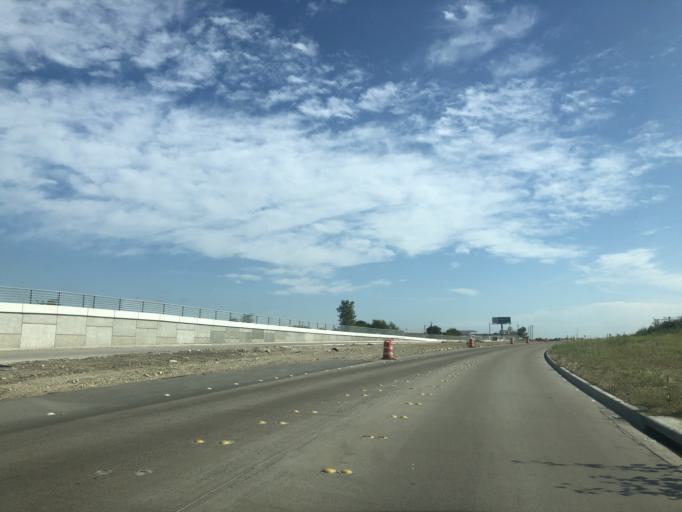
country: US
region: Texas
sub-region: Denton County
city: Justin
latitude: 33.0542
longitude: -97.3014
